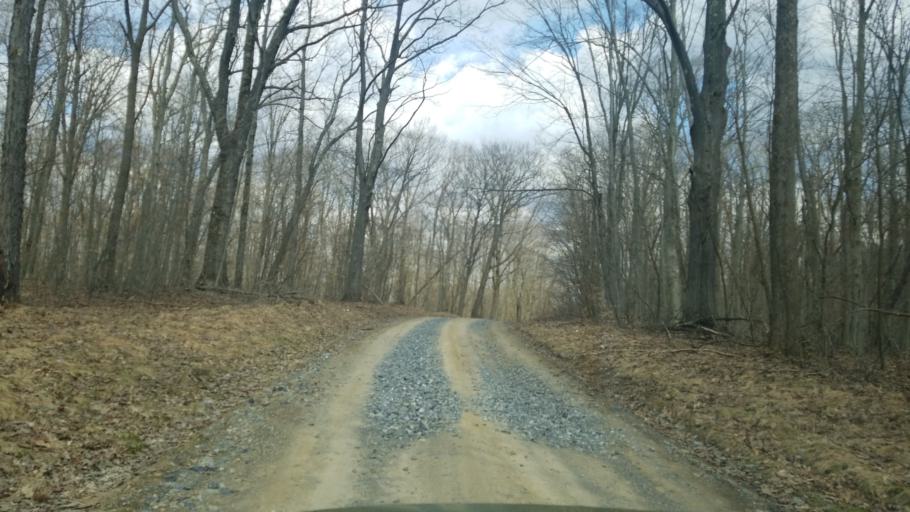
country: US
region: Pennsylvania
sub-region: Clearfield County
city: Clearfield
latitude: 41.1557
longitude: -78.5164
